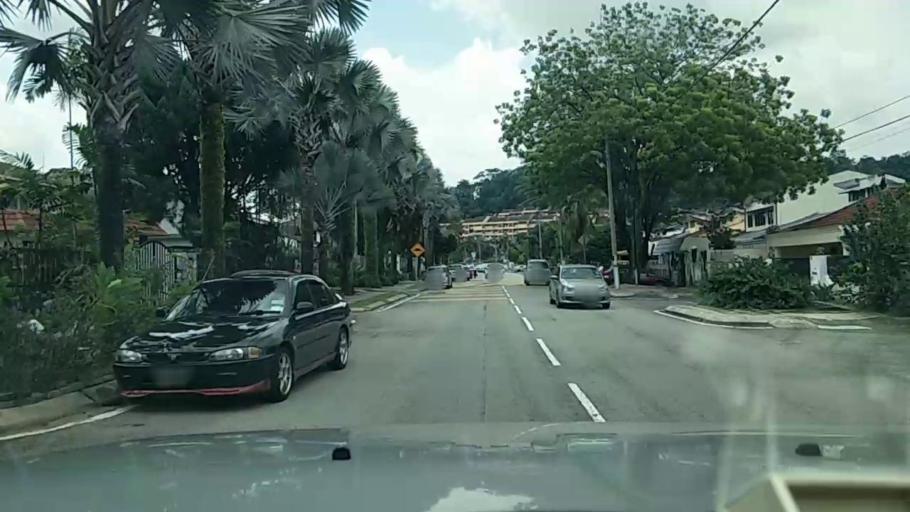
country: MY
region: Kuala Lumpur
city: Kuala Lumpur
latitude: 3.1359
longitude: 101.6734
